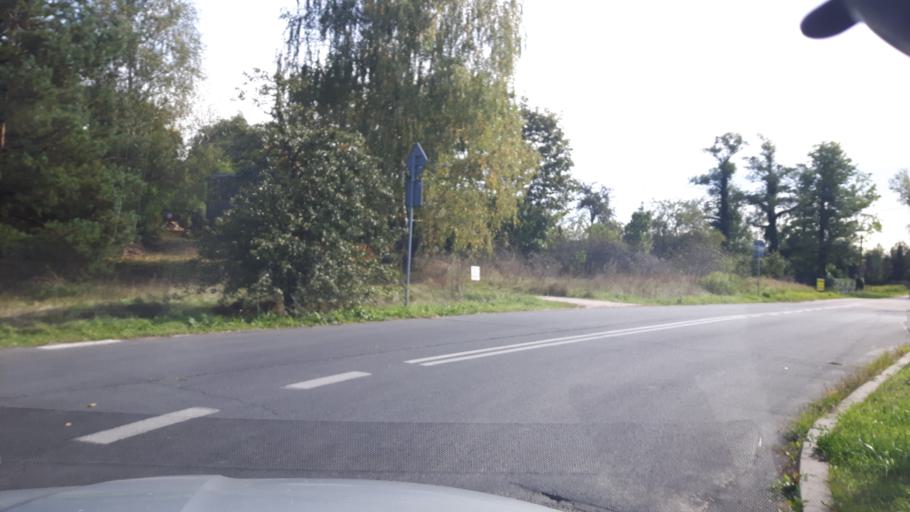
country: PL
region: Masovian Voivodeship
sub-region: Powiat legionowski
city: Stanislawow Pierwszy
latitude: 52.3620
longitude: 21.0623
